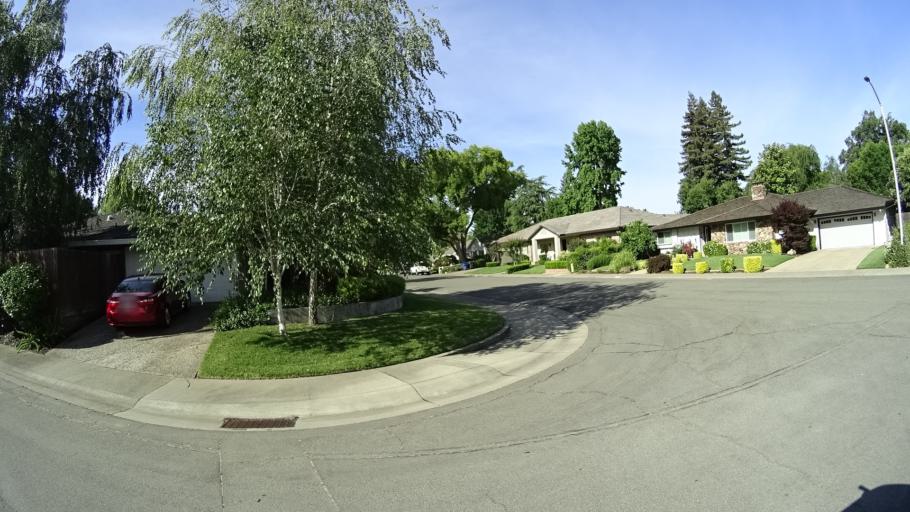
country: US
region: California
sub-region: Sacramento County
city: Rosemont
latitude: 38.5666
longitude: -121.4010
